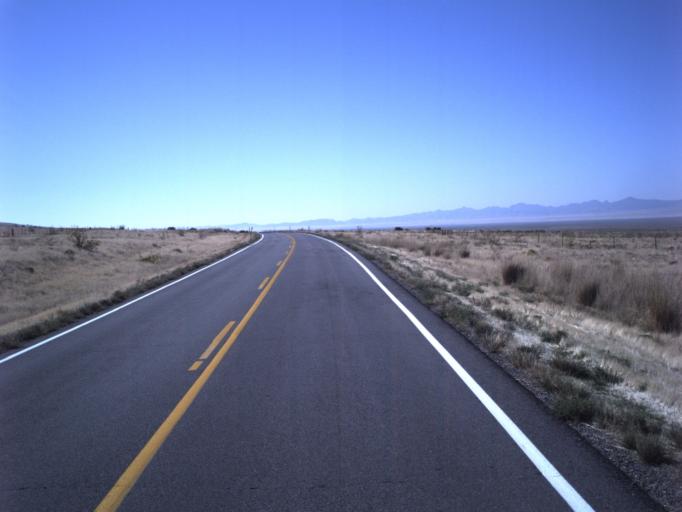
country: US
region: Utah
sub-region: Tooele County
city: Grantsville
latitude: 40.5915
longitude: -112.7201
